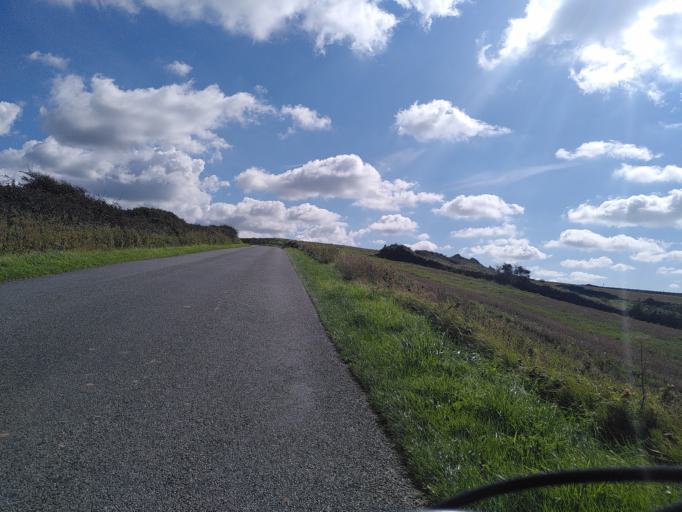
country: FR
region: Nord-Pas-de-Calais
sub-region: Departement du Pas-de-Calais
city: Wimille
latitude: 50.7770
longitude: 1.6287
